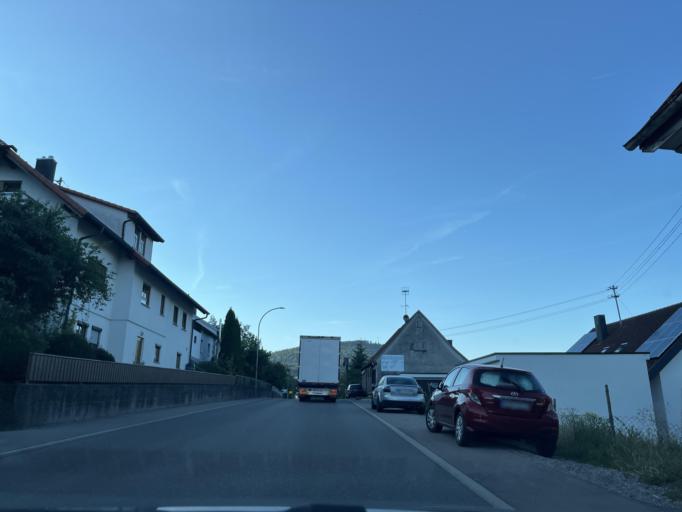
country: DE
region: Baden-Wuerttemberg
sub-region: Tuebingen Region
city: Jungingen
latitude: 48.3051
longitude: 9.0658
